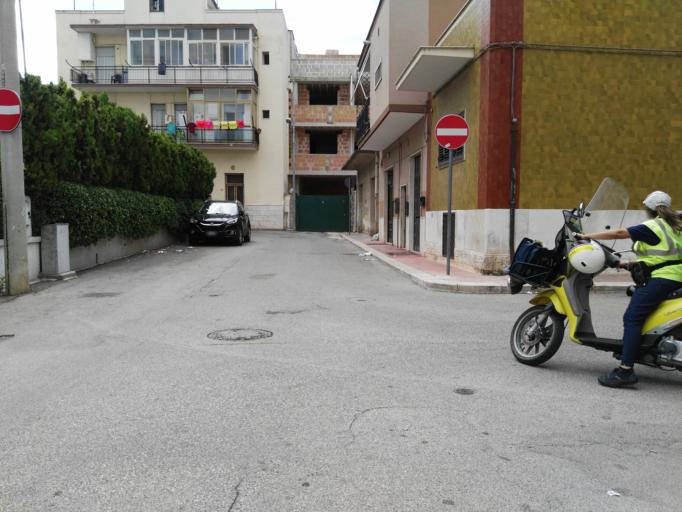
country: IT
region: Apulia
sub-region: Provincia di Bari
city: Triggiano
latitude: 41.0635
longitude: 16.9157
